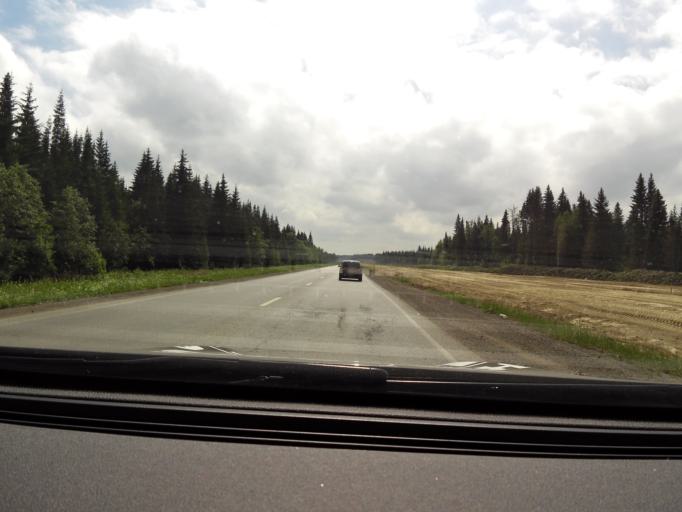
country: RU
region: Perm
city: Kukushtan
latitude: 57.6547
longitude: 56.4424
